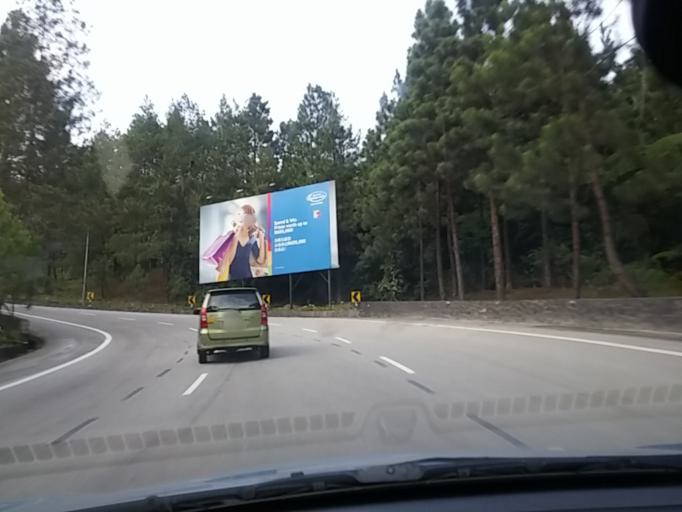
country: MY
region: Pahang
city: Kampung Bukit Tinggi, Bentong
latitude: 3.4159
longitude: 101.7850
